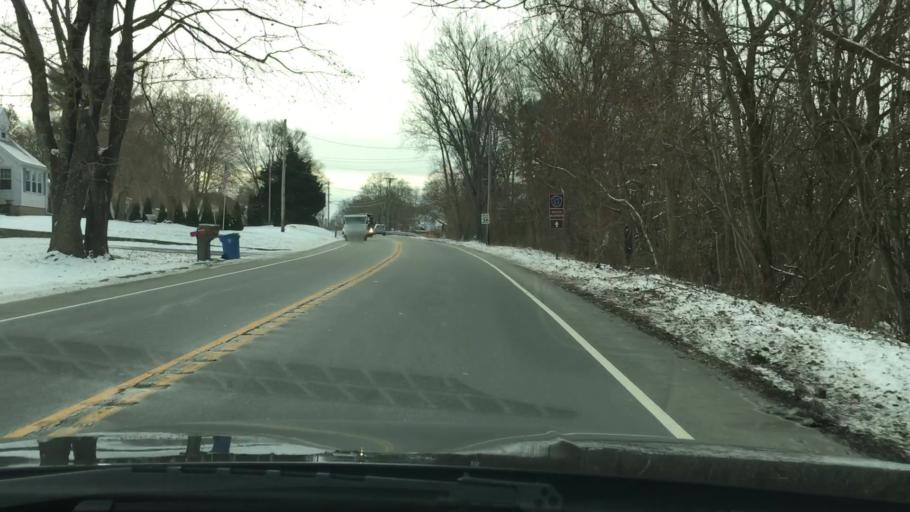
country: US
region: Connecticut
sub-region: New London County
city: Norwich
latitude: 41.5018
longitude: -72.0769
